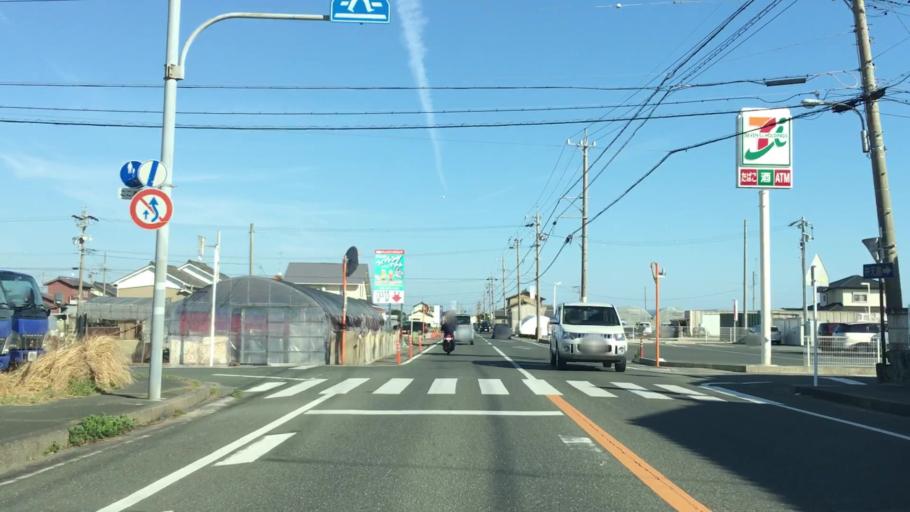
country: JP
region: Shizuoka
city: Kosai-shi
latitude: 34.7003
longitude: 137.6185
